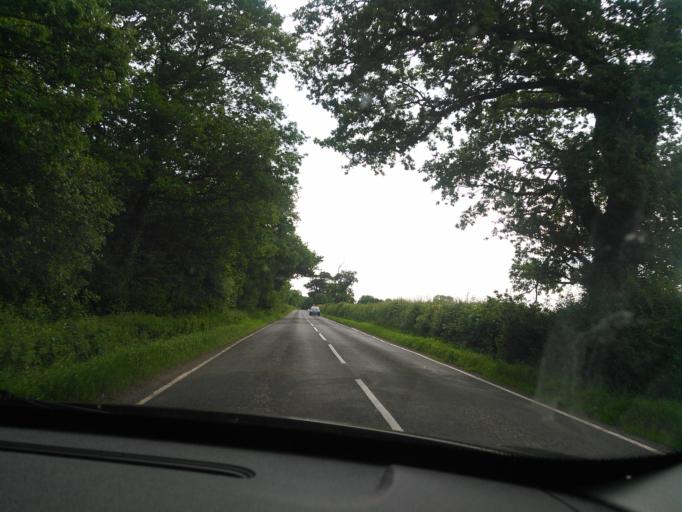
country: GB
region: England
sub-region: Shropshire
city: Shawbury
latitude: 52.7398
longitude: -2.6586
